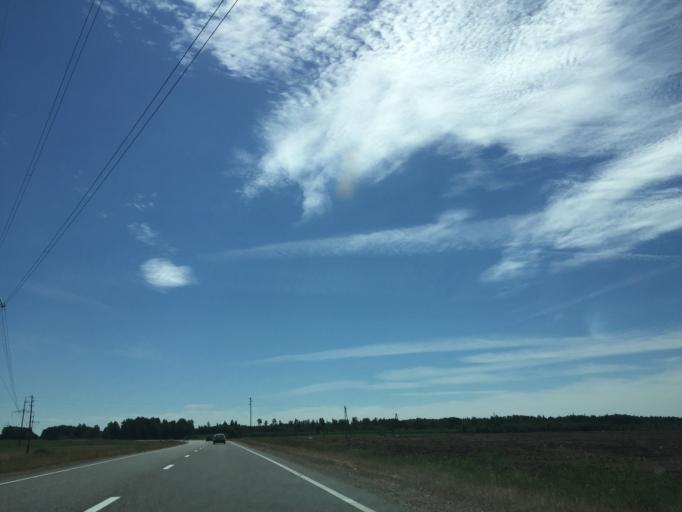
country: LV
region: Broceni
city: Broceni
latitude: 56.6640
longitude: 22.5997
